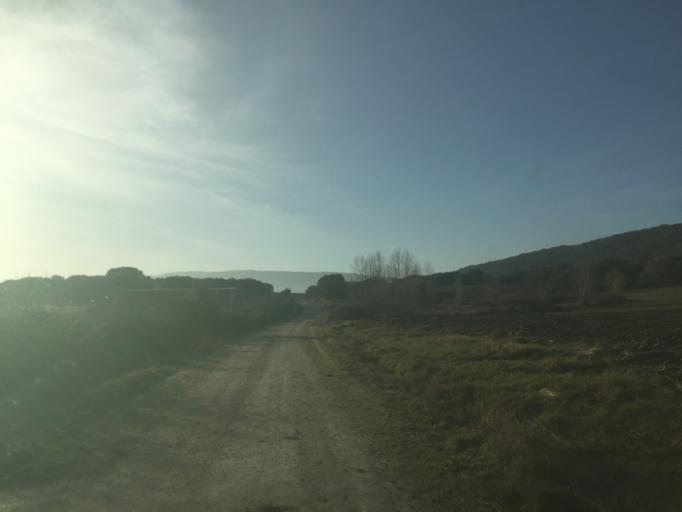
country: ES
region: Castille and Leon
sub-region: Provincia de Burgos
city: Medina de Pomar
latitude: 42.9267
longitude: -3.5937
